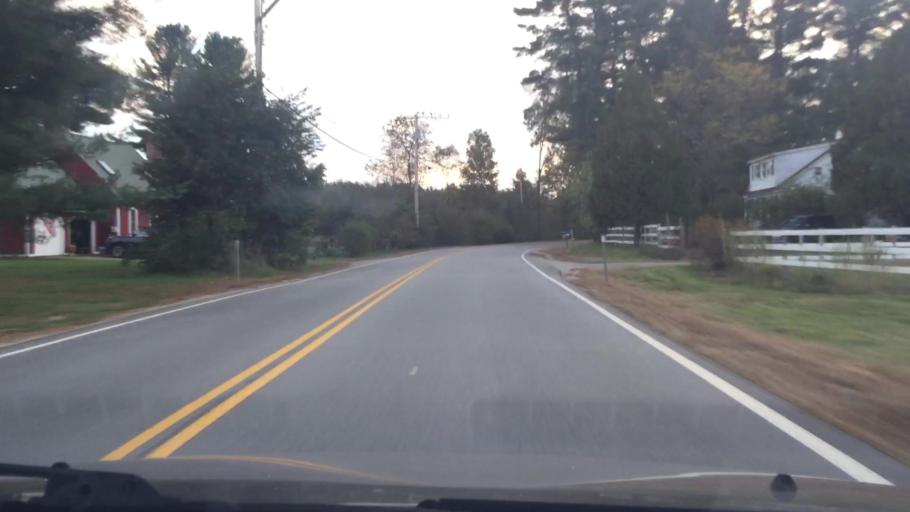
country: US
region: New Hampshire
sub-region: Cheshire County
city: Swanzey
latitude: 42.8533
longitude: -72.2776
